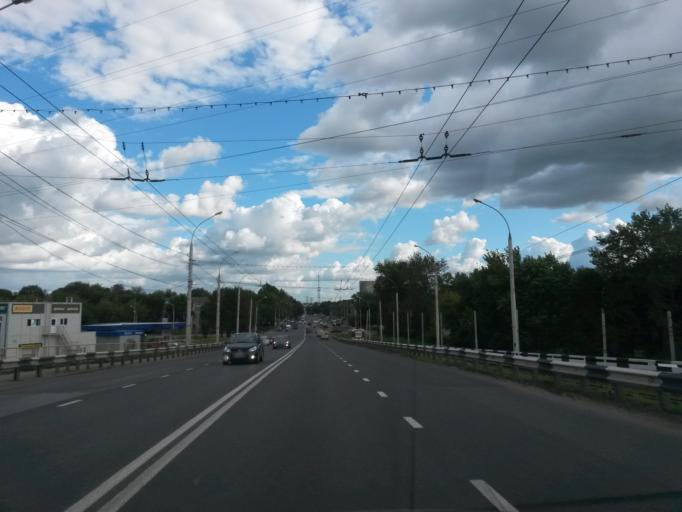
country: RU
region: Jaroslavl
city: Yaroslavl
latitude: 57.6430
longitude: 39.8543
